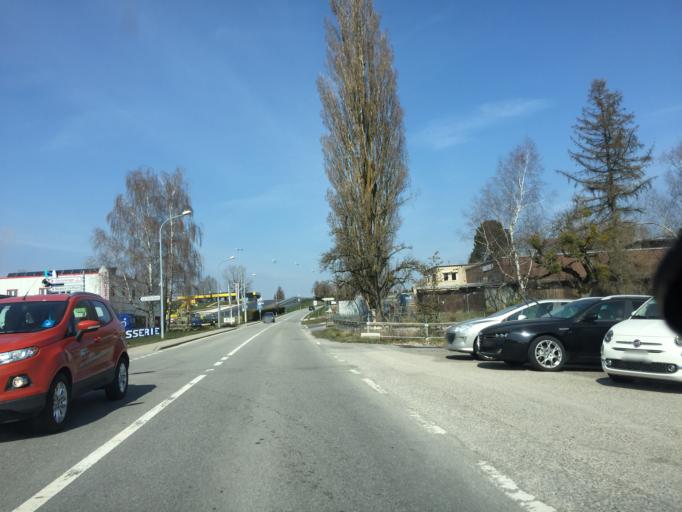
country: CH
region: Vaud
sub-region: Morges District
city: Cossonay
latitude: 46.6193
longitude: 6.5085
